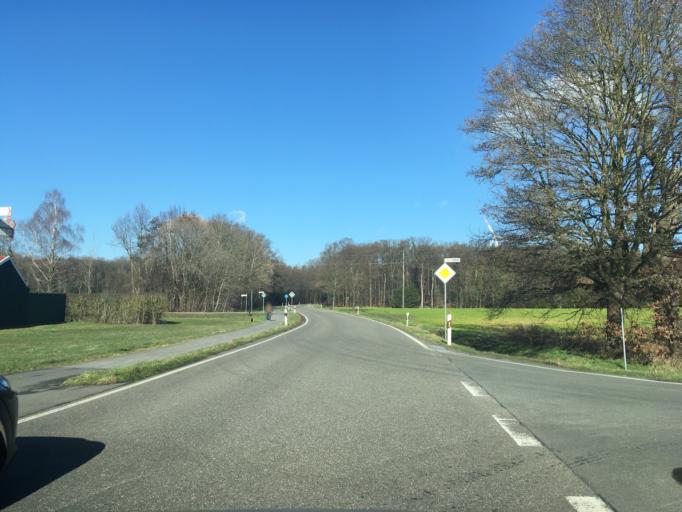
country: DE
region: North Rhine-Westphalia
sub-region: Regierungsbezirk Munster
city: Rhede
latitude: 51.8603
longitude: 6.6936
